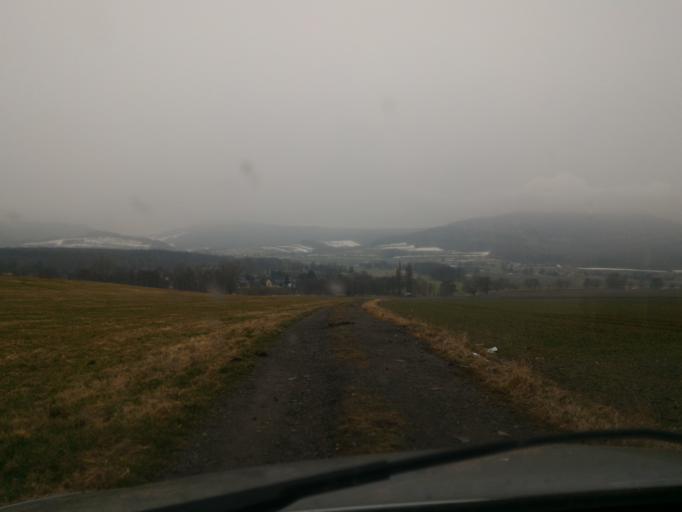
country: CZ
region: Ustecky
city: Varnsdorf
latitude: 50.8909
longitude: 14.6463
